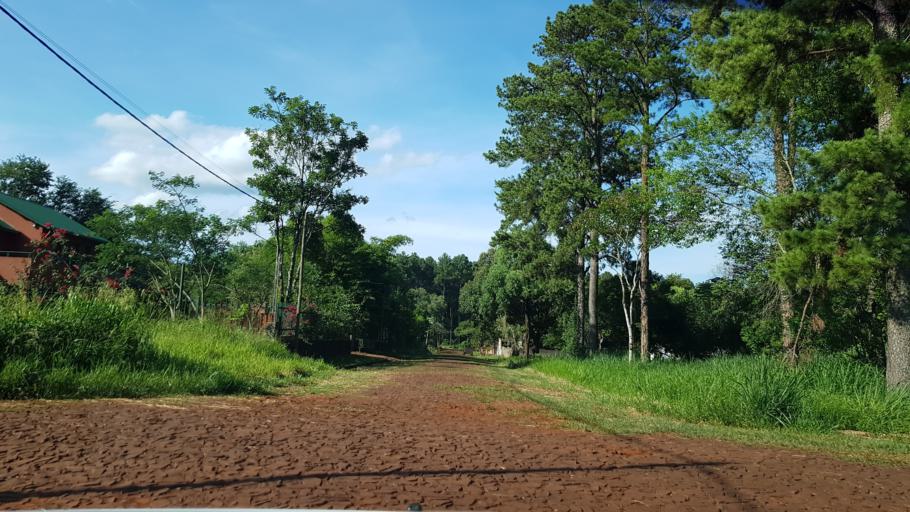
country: AR
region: Misiones
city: Puerto Libertad
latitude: -25.9190
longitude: -54.5764
